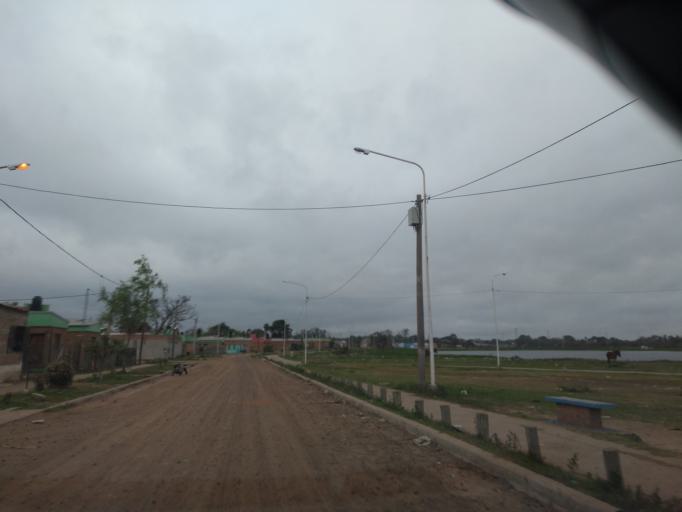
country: AR
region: Chaco
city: Resistencia
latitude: -27.4595
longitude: -58.9643
